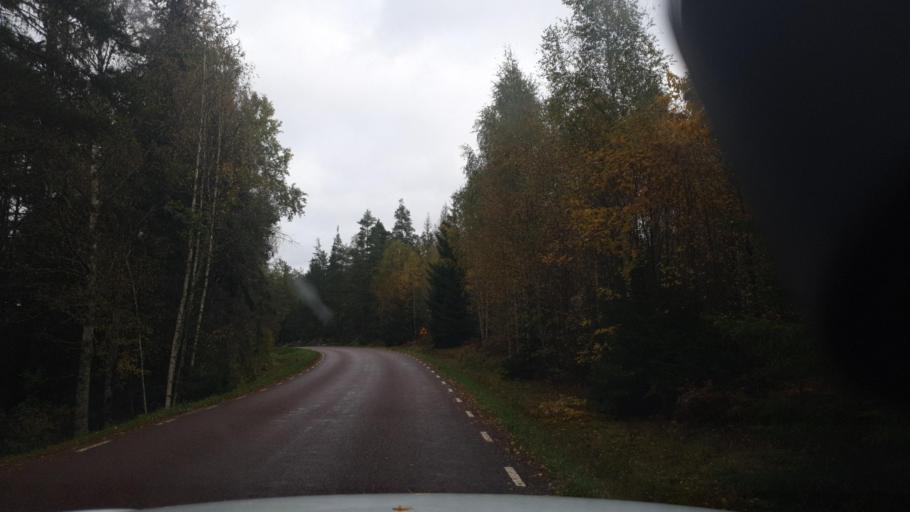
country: SE
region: Vaermland
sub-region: Grums Kommun
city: Grums
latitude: 59.4191
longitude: 13.0858
